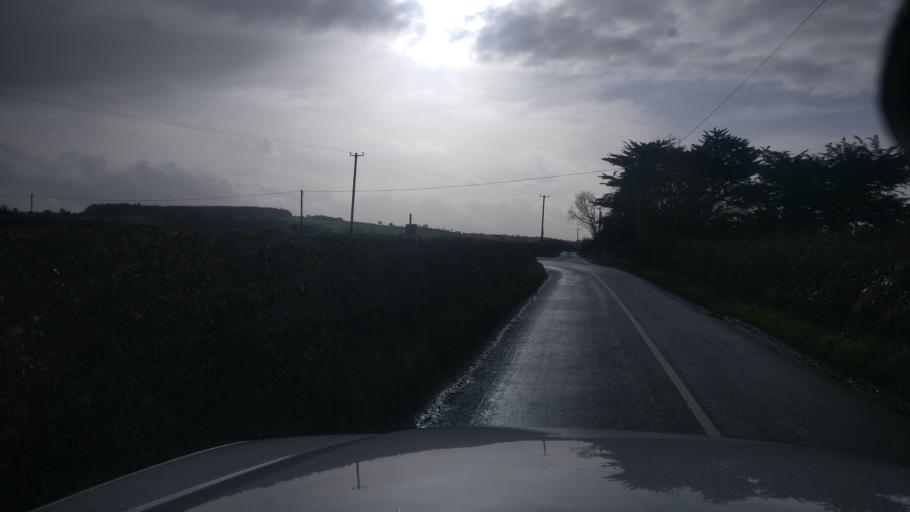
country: IE
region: Munster
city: Nenagh Bridge
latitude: 52.9617
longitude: -8.0831
